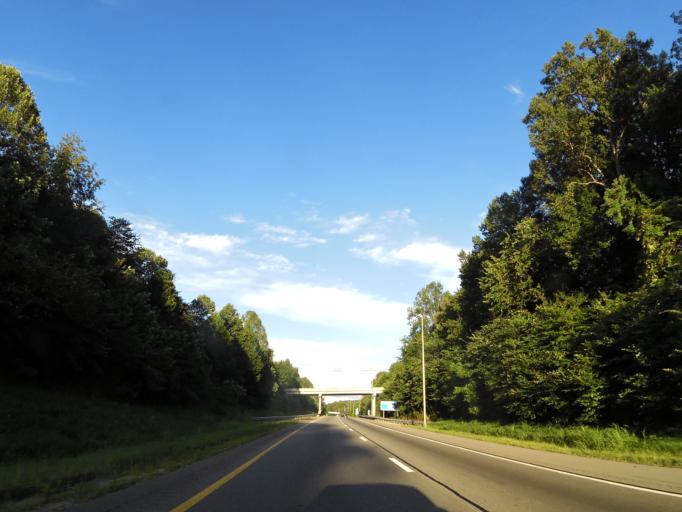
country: US
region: Tennessee
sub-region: Putnam County
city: Cookeville
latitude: 36.1371
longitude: -85.4895
